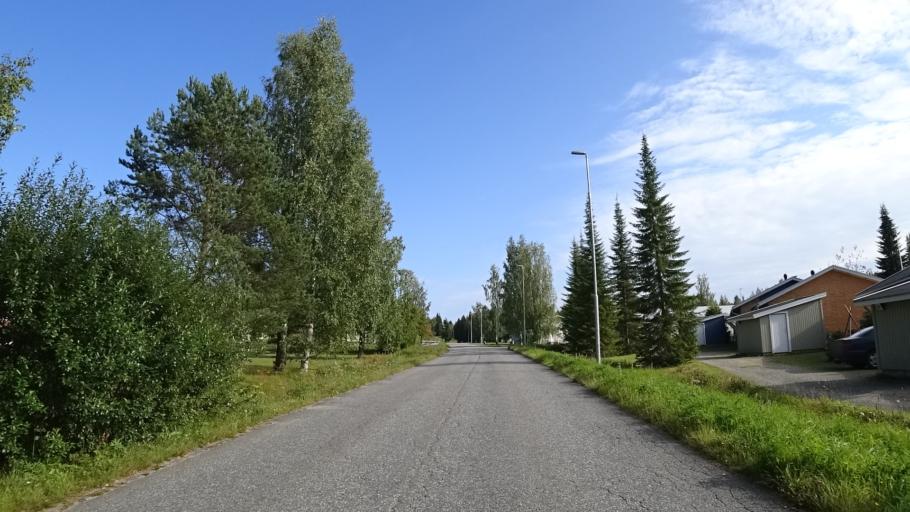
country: FI
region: North Karelia
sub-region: Joensuu
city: Eno
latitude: 62.7956
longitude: 30.1394
